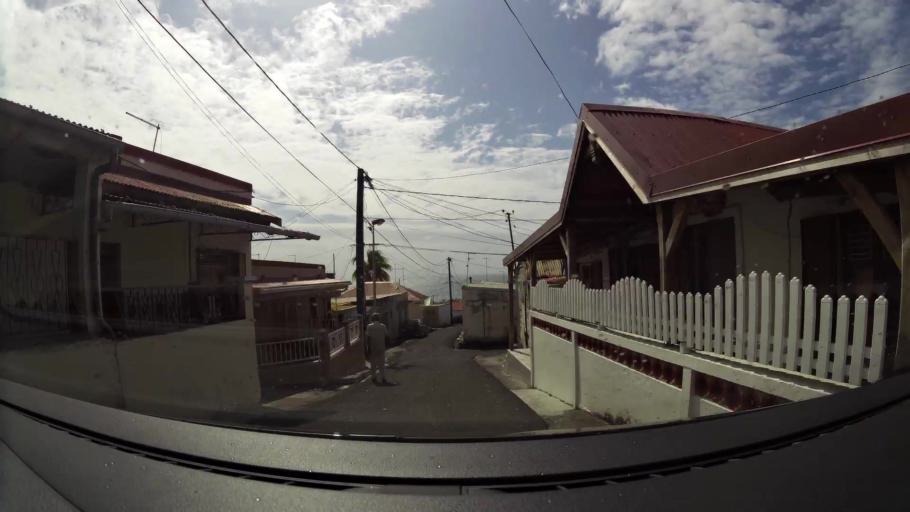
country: GP
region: Guadeloupe
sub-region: Guadeloupe
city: Basse-Terre
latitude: 16.0018
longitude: -61.7350
